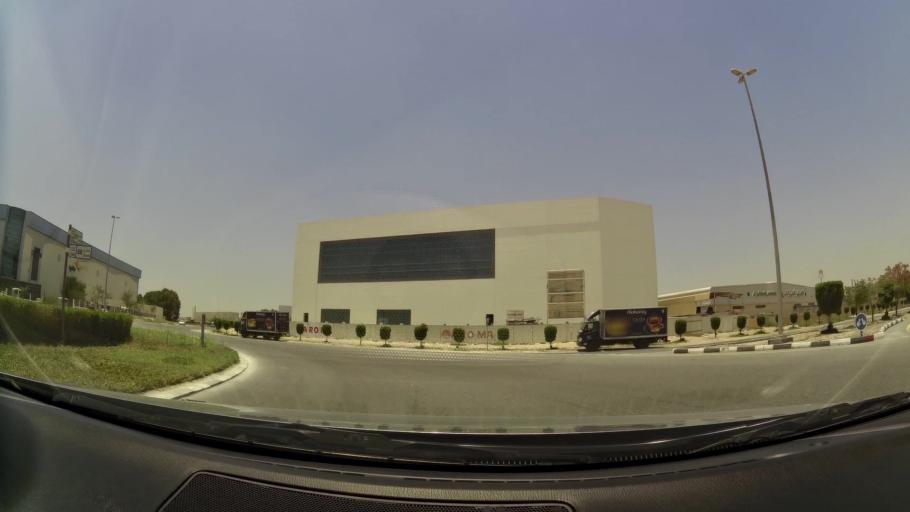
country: AE
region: Dubai
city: Dubai
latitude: 24.9827
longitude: 55.1726
